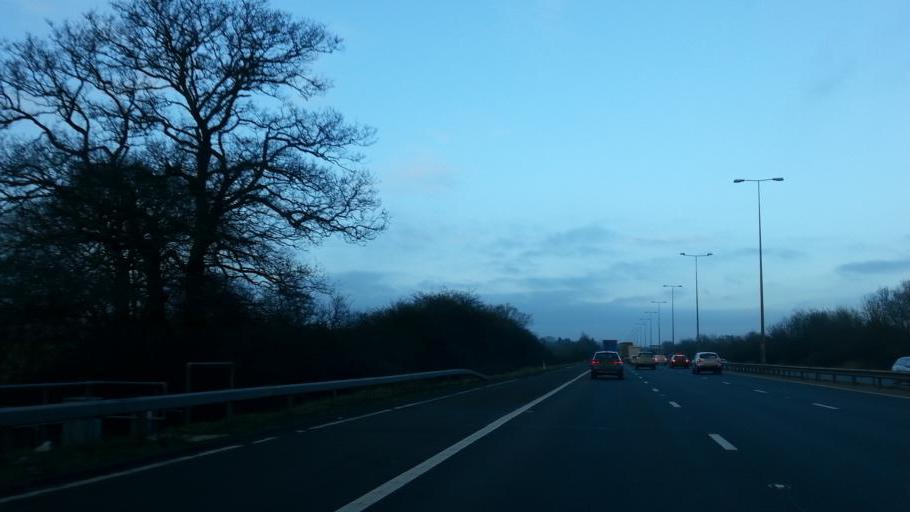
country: GB
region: England
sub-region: Worcestershire
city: Kempsey
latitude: 52.1414
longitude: -2.1958
